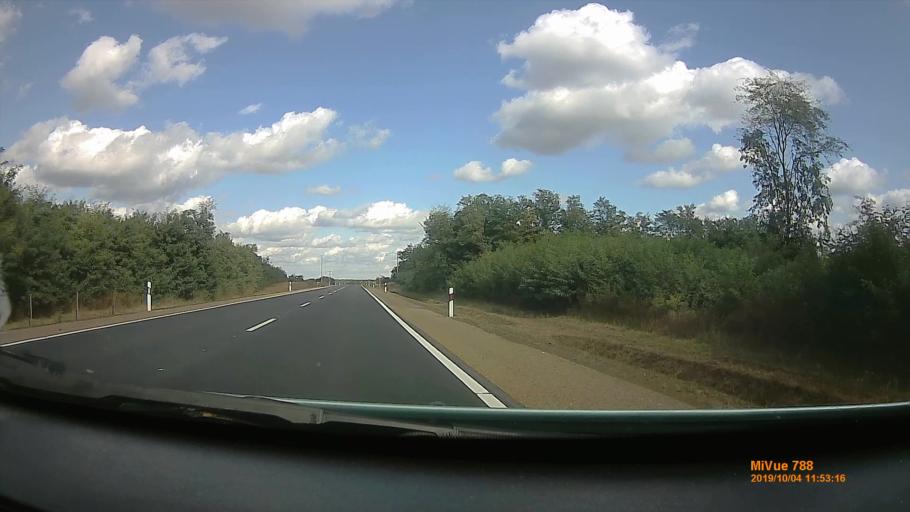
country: HU
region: Szabolcs-Szatmar-Bereg
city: Nyirtelek
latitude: 48.0076
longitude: 21.6751
